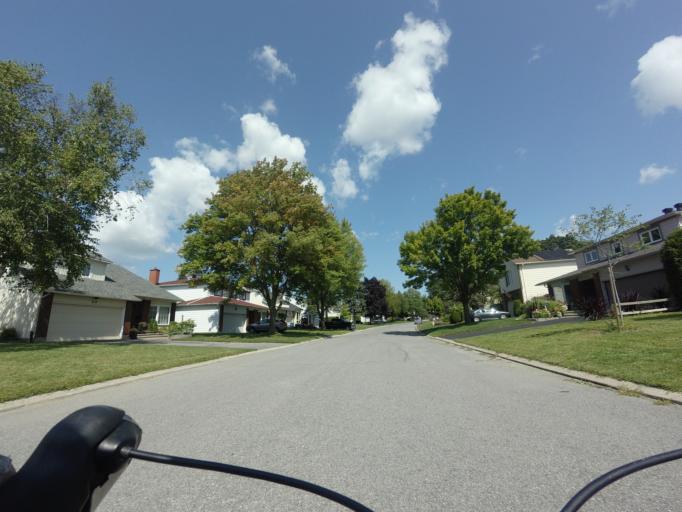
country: CA
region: Ontario
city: Bells Corners
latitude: 45.2866
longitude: -75.8661
